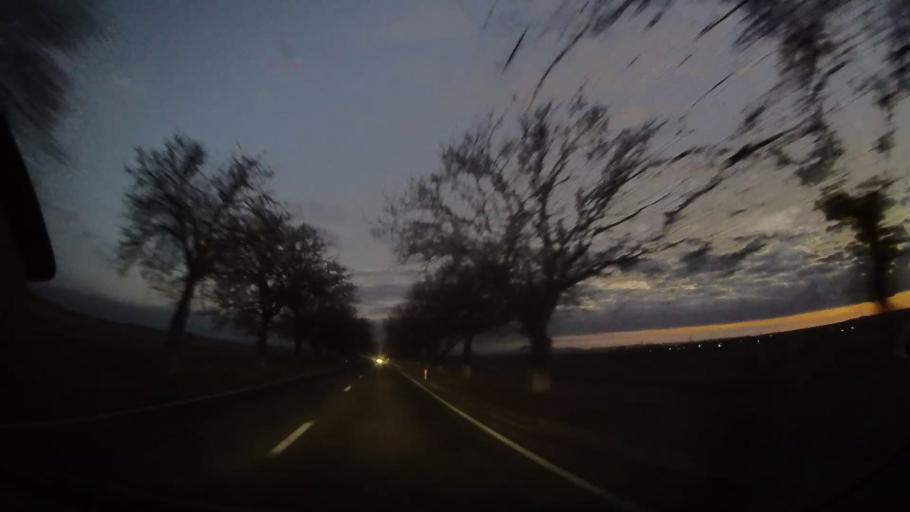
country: RO
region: Tulcea
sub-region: Comuna Frecatei
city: Cataloi
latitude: 45.0969
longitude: 28.7418
